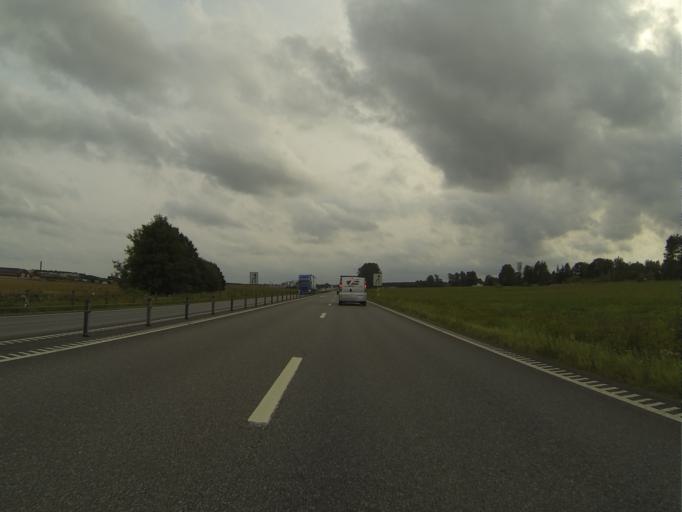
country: SE
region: Skane
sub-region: Kristianstads Kommun
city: Norra Asum
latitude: 55.9609
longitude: 14.0688
